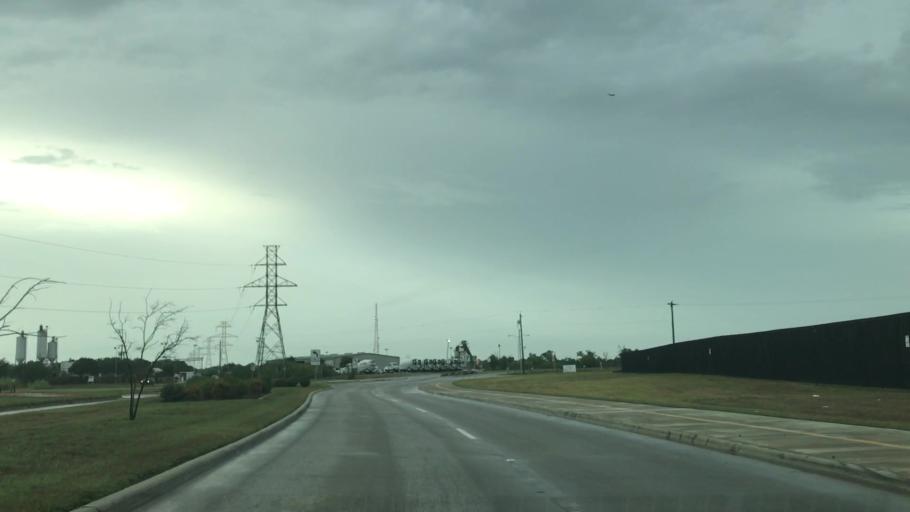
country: US
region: Texas
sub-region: Denton County
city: Lewisville
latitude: 33.0481
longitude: -96.9792
